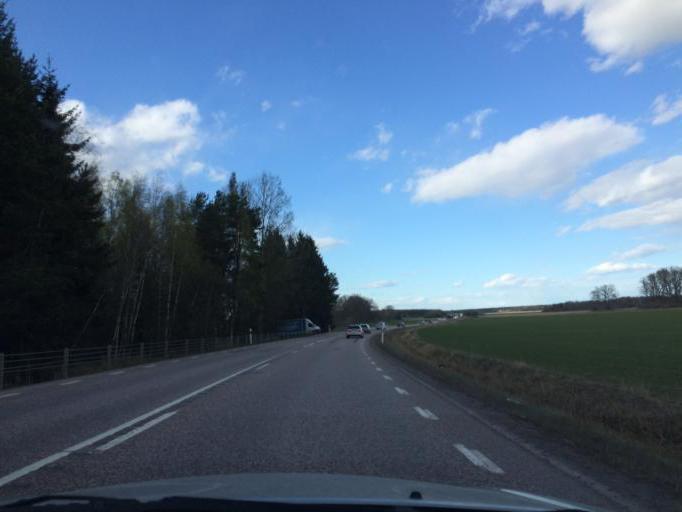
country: SE
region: Vaestmanland
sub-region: Hallstahammars Kommun
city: Kolback
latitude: 59.5350
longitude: 16.3210
